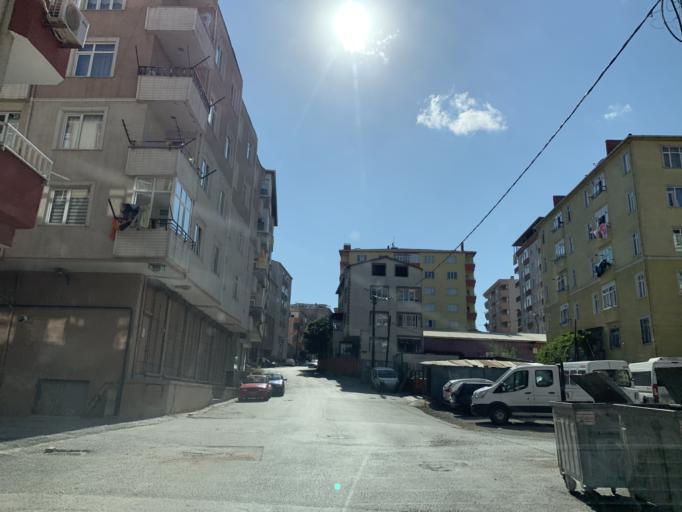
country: TR
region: Istanbul
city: Pendik
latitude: 40.8724
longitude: 29.2774
